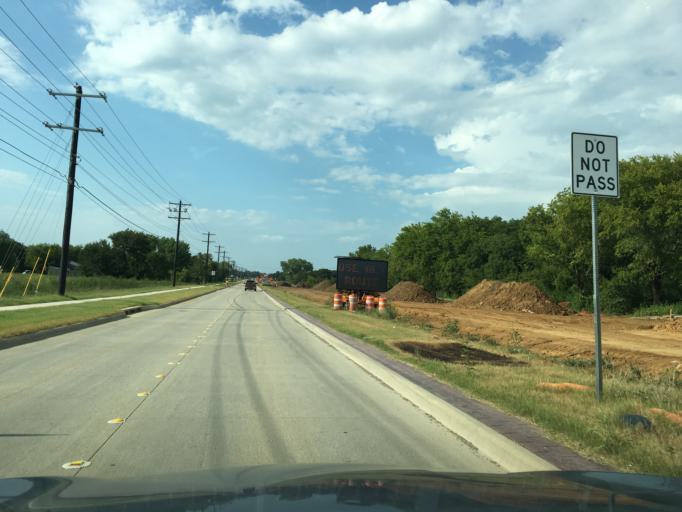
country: US
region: Texas
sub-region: Denton County
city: Denton
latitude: 33.2202
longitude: -97.0835
